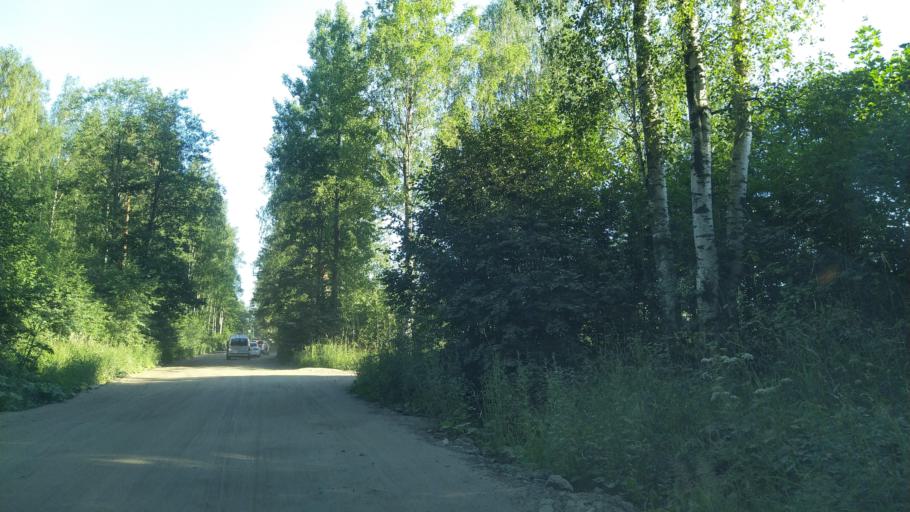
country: RU
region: Leningrad
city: Koltushi
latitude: 59.9157
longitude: 30.7347
